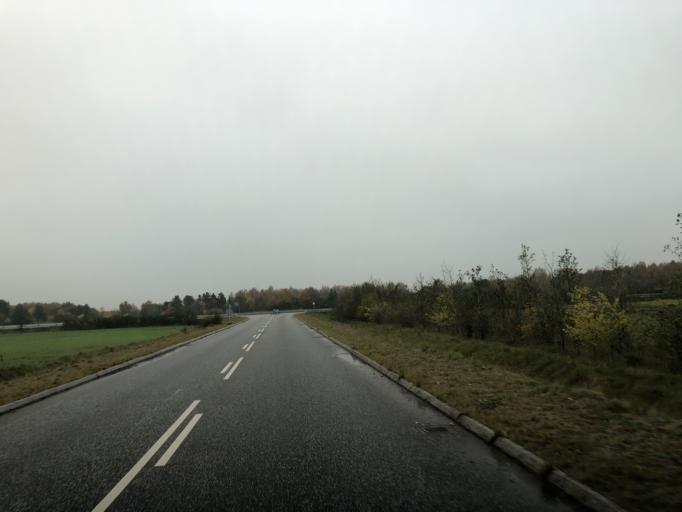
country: DK
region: Central Jutland
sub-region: Herning Kommune
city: Sunds
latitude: 56.2048
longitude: 8.9956
